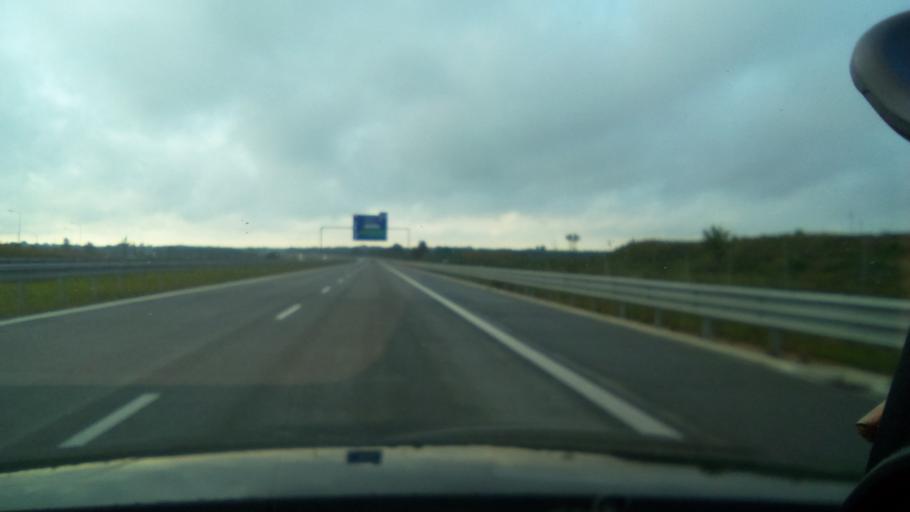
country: PL
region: Silesian Voivodeship
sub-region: Powiat czestochowski
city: Konopiska
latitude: 50.7584
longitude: 19.0241
